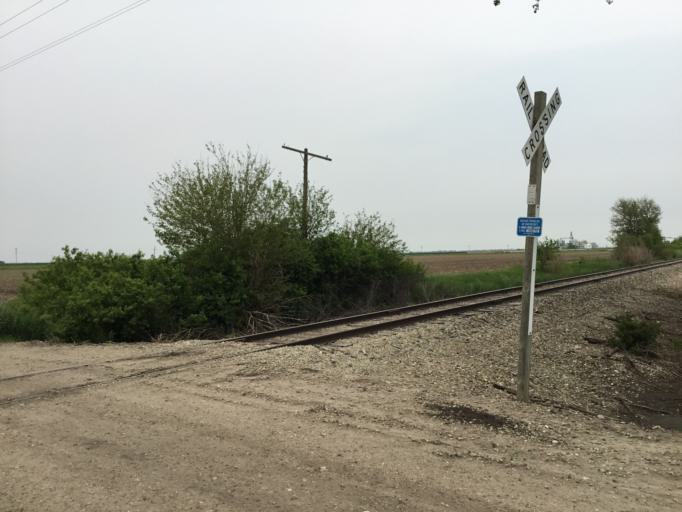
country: US
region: Kansas
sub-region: Republic County
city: Belleville
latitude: 39.7823
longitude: -97.8385
